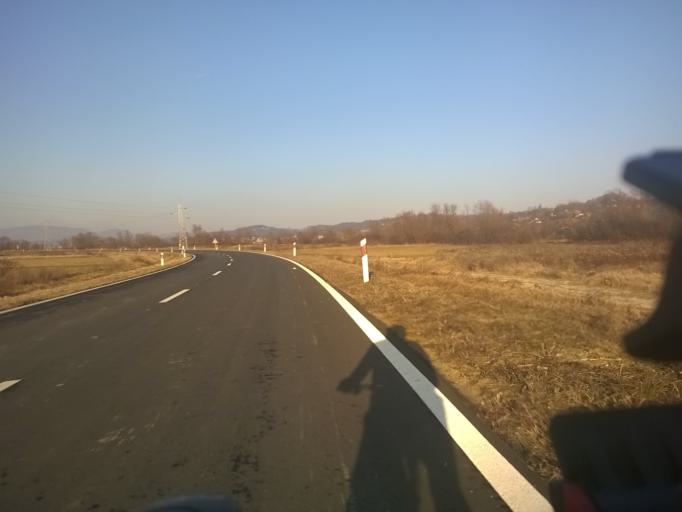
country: HR
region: Krapinsko-Zagorska
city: Zabok
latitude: 46.0331
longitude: 15.9214
